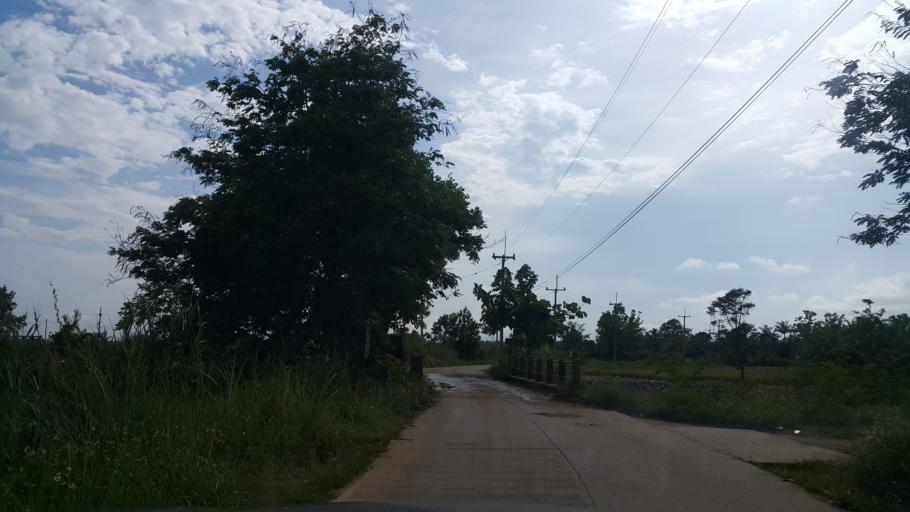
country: TH
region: Chiang Rai
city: Chiang Rai
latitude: 19.9714
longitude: 99.8972
